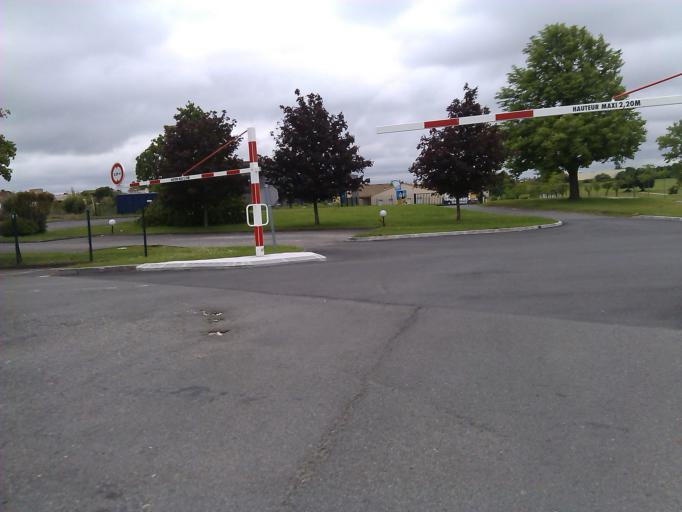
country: FR
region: Poitou-Charentes
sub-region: Departement de la Charente
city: Barbezieux-Saint-Hilaire
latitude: 45.4754
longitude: -0.1615
